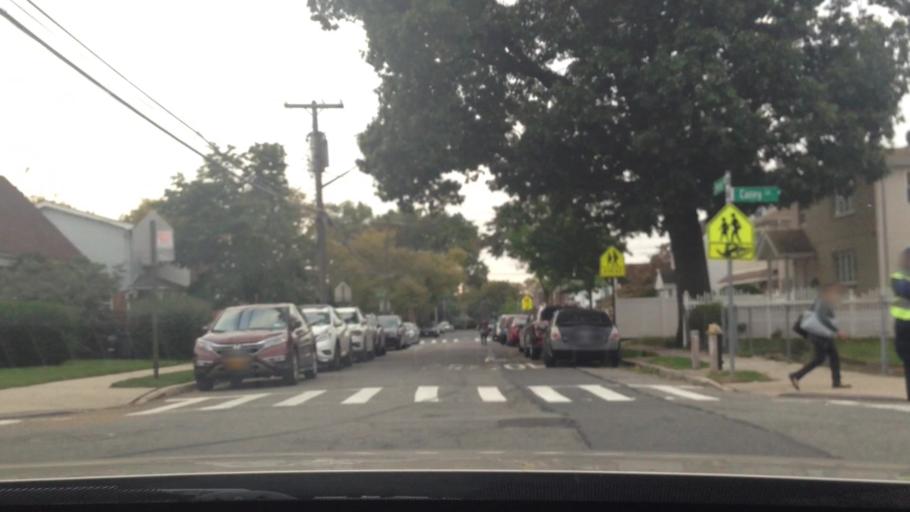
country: US
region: New York
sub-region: Nassau County
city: South Valley Stream
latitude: 40.6607
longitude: -73.7337
